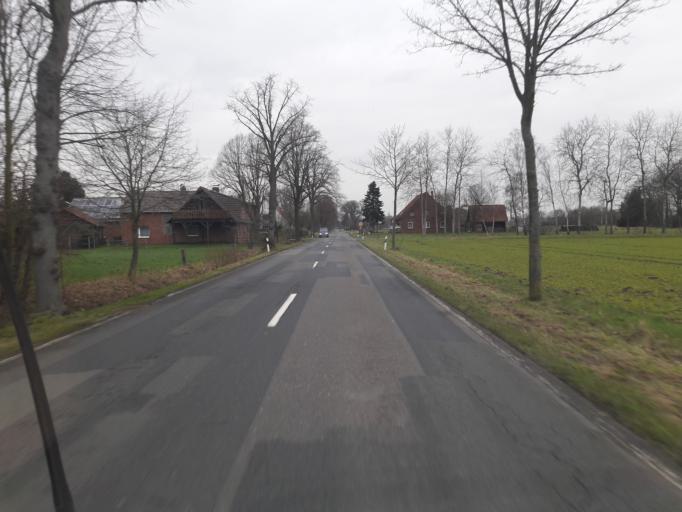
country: DE
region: Lower Saxony
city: Warmsen
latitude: 52.3900
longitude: 8.8537
